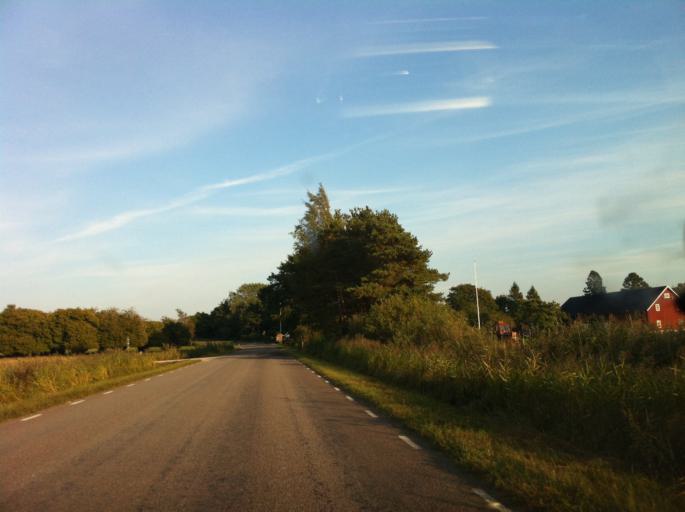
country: SE
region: Gotland
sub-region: Gotland
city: Slite
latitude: 57.4189
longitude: 18.8752
